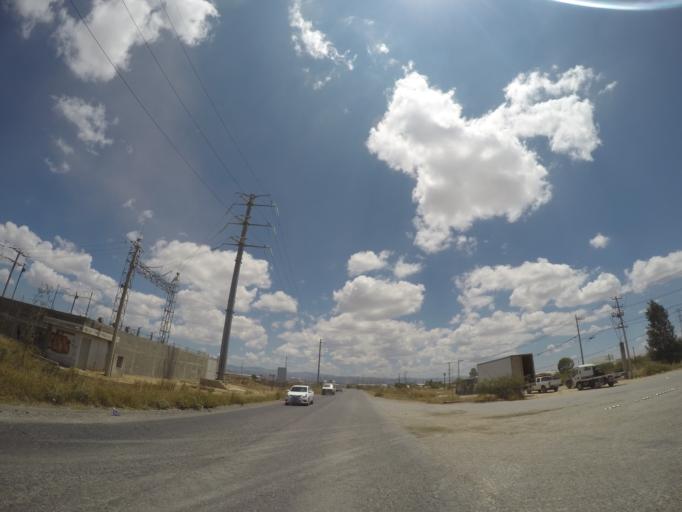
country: MX
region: San Luis Potosi
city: La Pila
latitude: 22.0413
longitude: -100.8894
